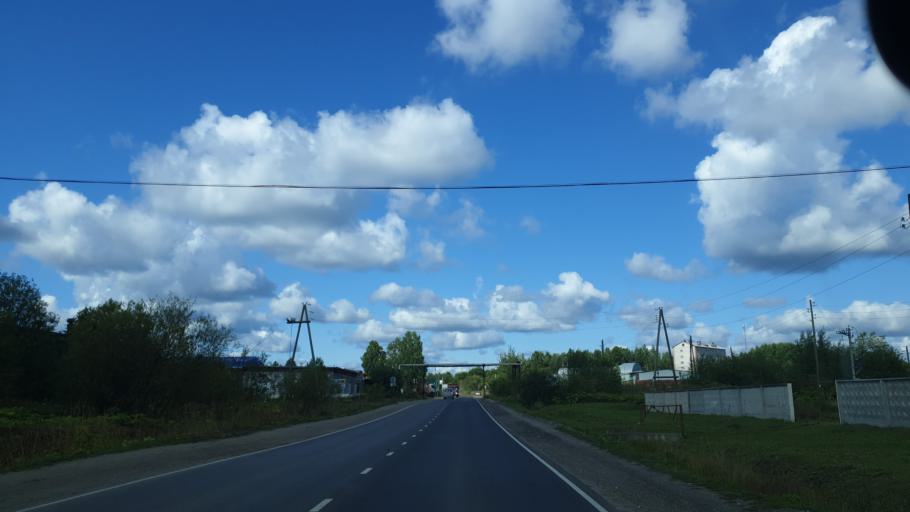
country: RU
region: Komi Republic
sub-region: Syktyvdinskiy Rayon
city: Syktyvkar
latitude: 61.6402
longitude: 50.7974
